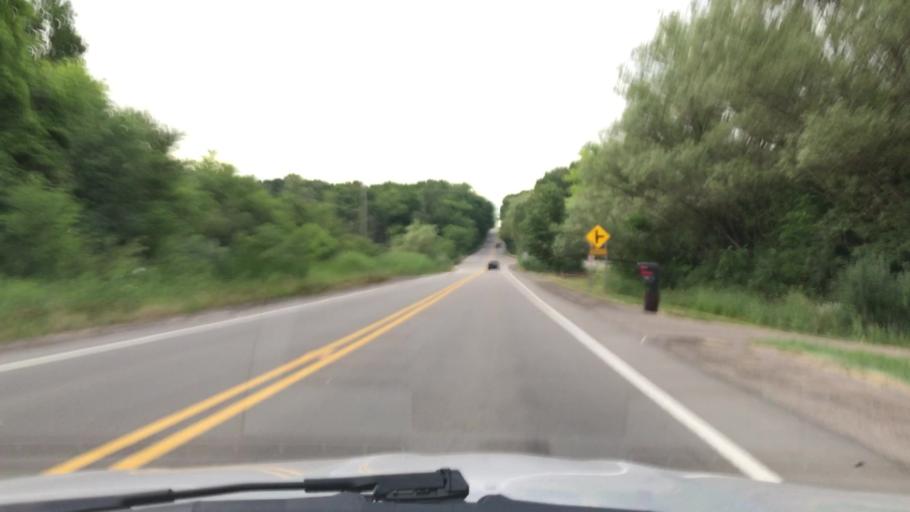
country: US
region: Michigan
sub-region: Wayne County
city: Northville
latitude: 42.4285
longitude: -83.5120
